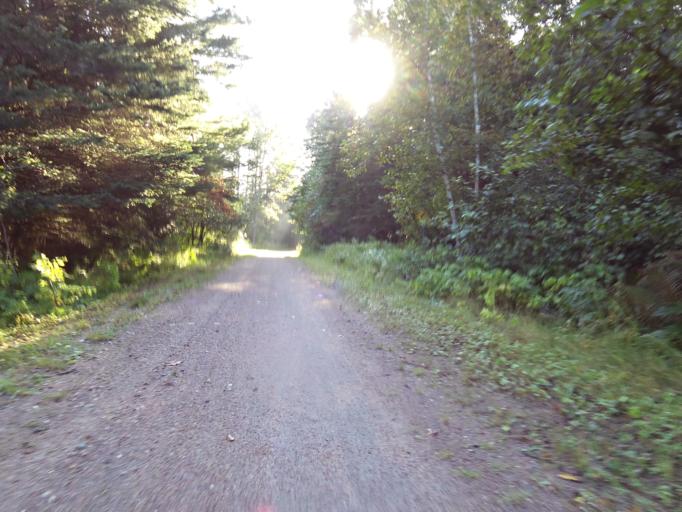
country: CA
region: Quebec
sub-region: Outaouais
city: Maniwaki
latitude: 46.2785
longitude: -76.0171
